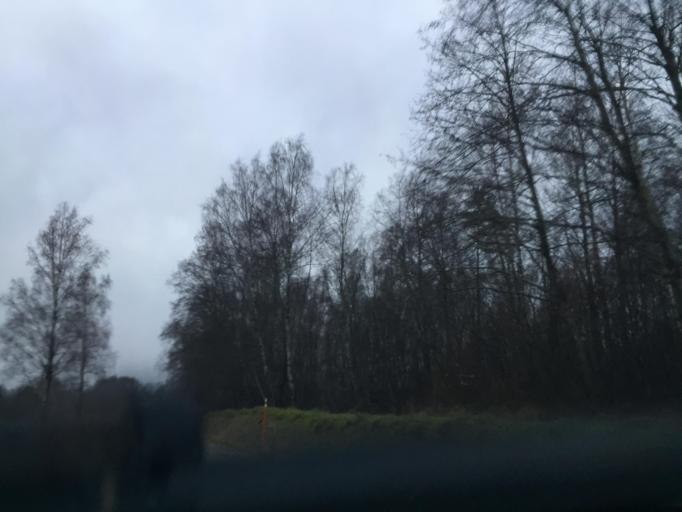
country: LV
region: Salacgrivas
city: Salacgriva
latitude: 57.7650
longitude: 24.4682
